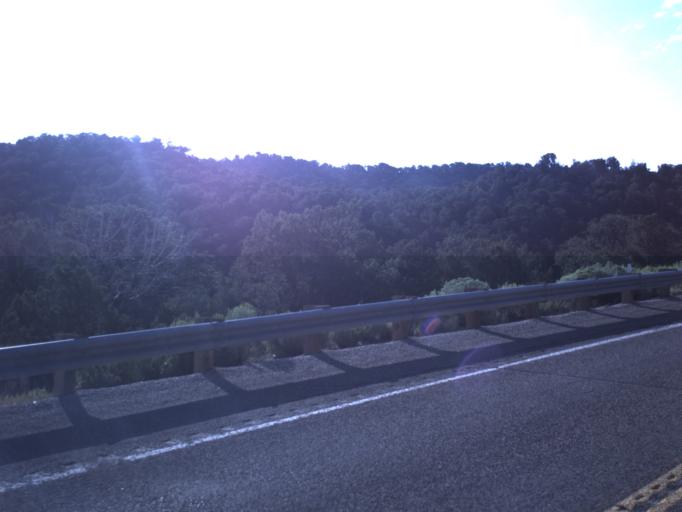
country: US
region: Utah
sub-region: Wayne County
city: Loa
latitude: 38.7232
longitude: -111.3986
